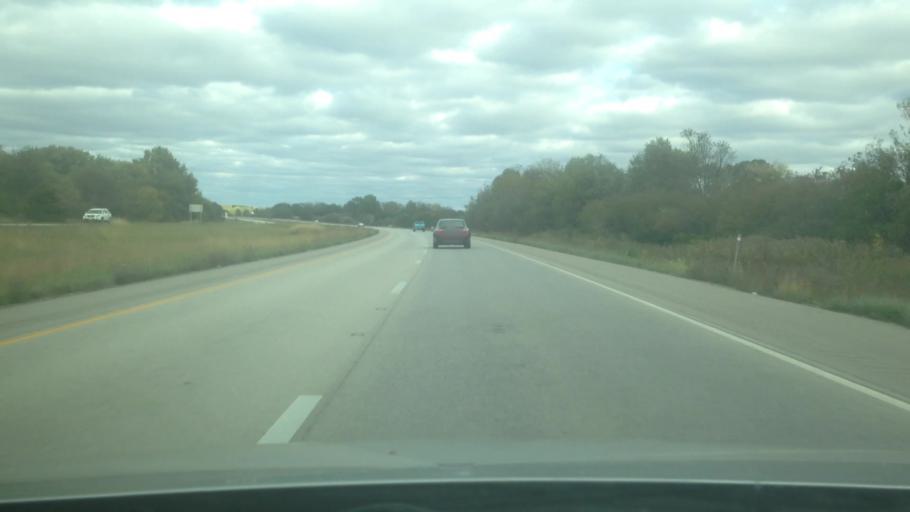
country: US
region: Illinois
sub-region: Macon County
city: Forsyth
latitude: 39.9109
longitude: -88.8771
